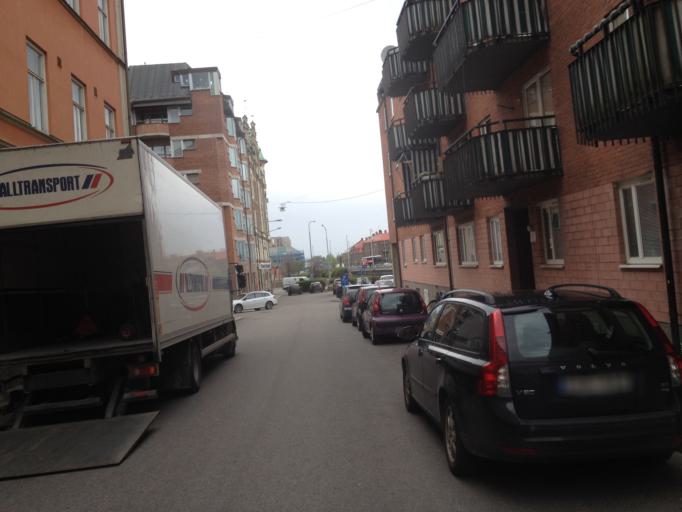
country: SE
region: OEstergoetland
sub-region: Norrkopings Kommun
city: Norrkoping
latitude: 58.5928
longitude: 16.1940
